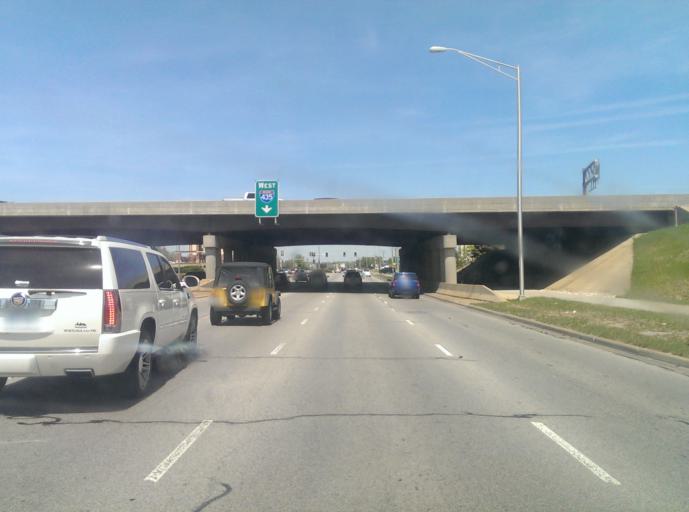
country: US
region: Kansas
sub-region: Johnson County
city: Overland Park
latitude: 38.9311
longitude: -94.6676
